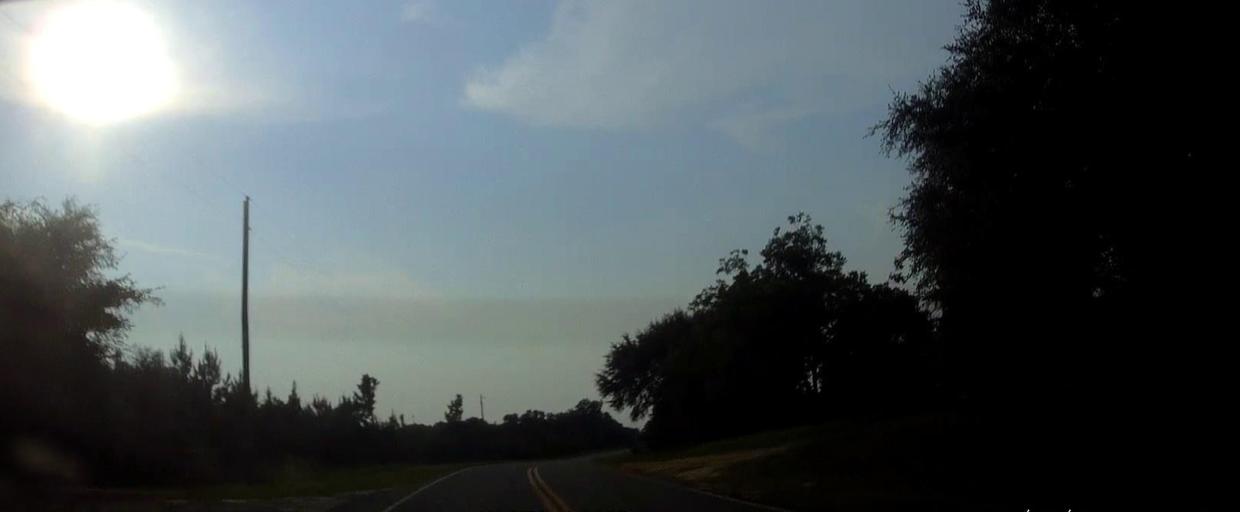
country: US
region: Georgia
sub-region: Laurens County
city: Dublin
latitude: 32.4855
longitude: -82.9744
